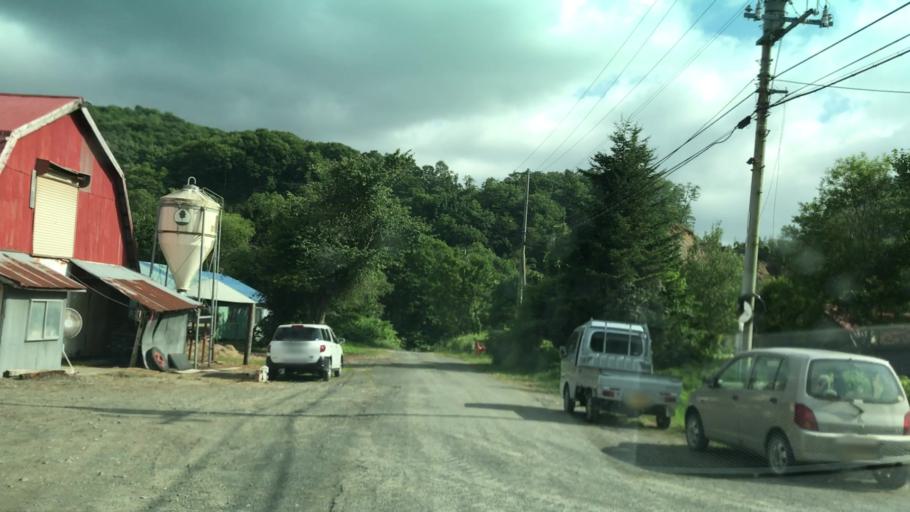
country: JP
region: Hokkaido
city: Shizunai-furukawacho
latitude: 42.7990
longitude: 142.3976
